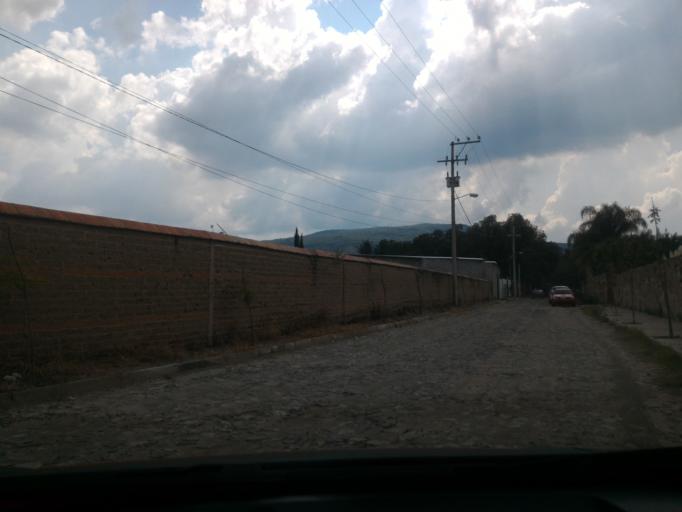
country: MX
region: Jalisco
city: Nuevo Mexico
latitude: 20.7007
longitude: -103.4716
